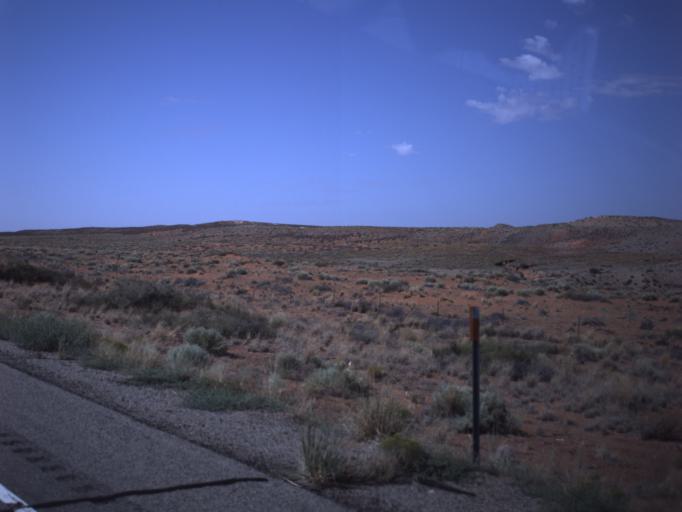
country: US
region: Utah
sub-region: San Juan County
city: Blanding
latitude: 37.2337
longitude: -109.6129
